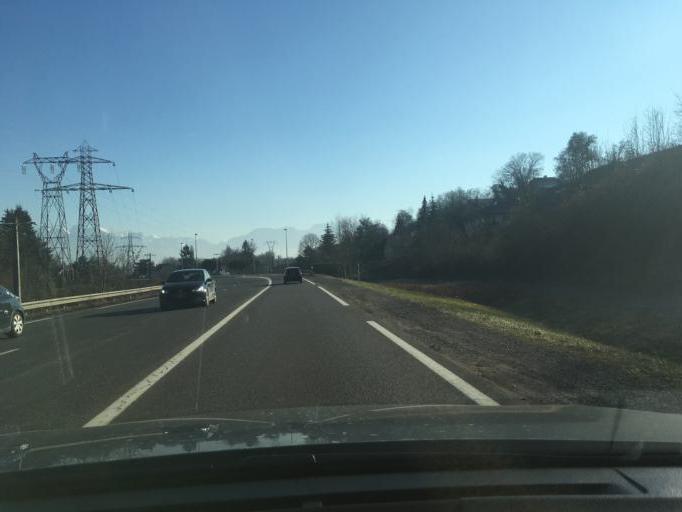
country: FR
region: Rhone-Alpes
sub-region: Departement de la Haute-Savoie
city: Cranves-Sales
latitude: 46.1926
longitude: 6.2927
